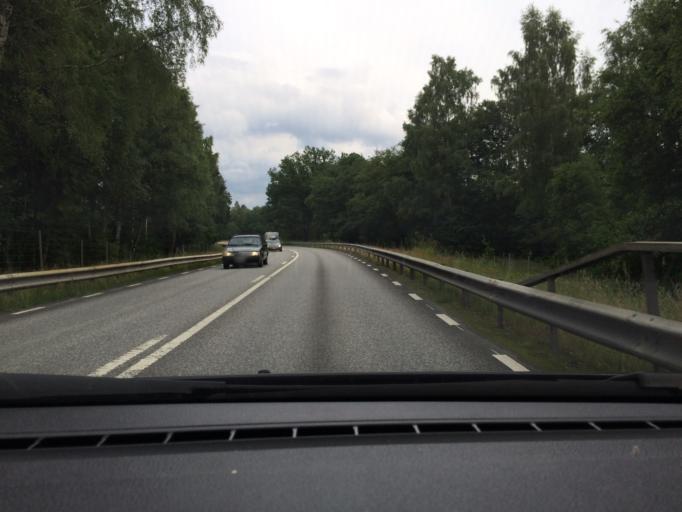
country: SE
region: Joenkoeping
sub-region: Varnamo Kommun
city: Forsheda
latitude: 57.1623
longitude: 13.8525
